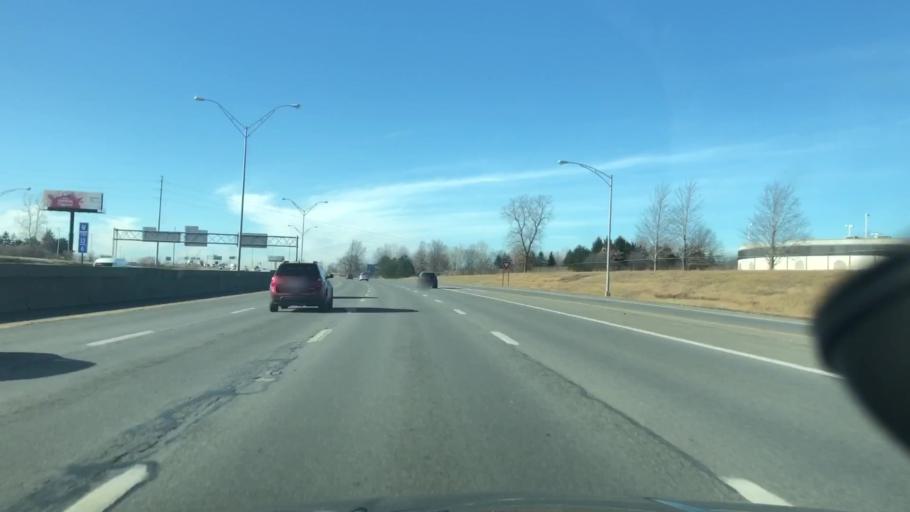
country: US
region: Ohio
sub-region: Cuyahoga County
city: Brooklyn
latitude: 41.4264
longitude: -81.7644
